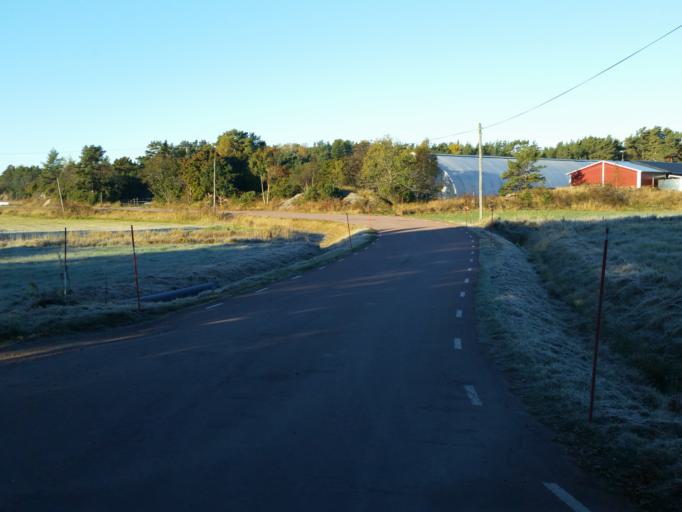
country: AX
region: Alands skaergard
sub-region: Vardoe
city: Vardoe
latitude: 60.2464
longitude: 20.3876
